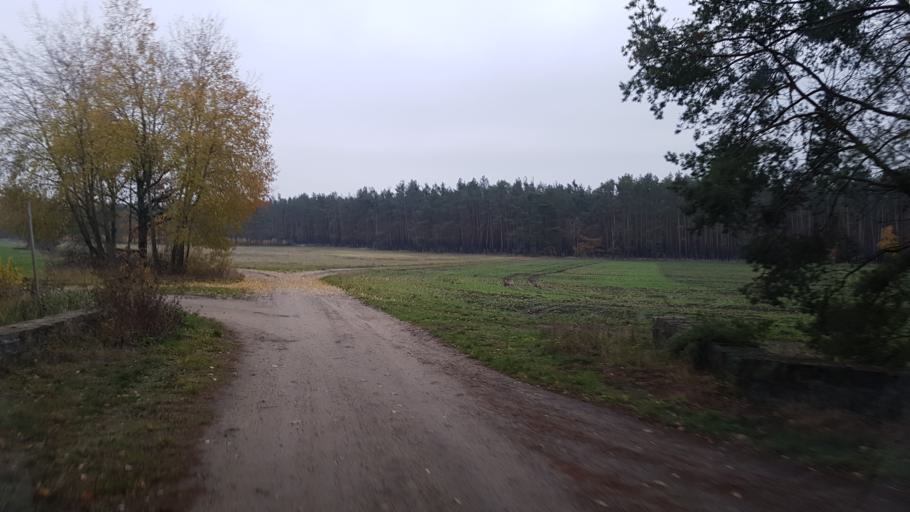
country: DE
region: Brandenburg
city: Schilda
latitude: 51.6392
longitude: 13.3977
